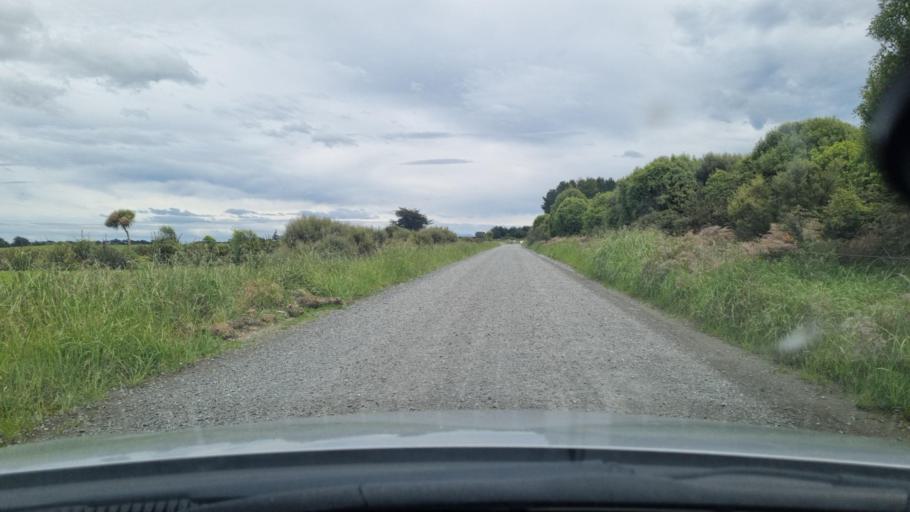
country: NZ
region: Southland
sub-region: Invercargill City
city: Invercargill
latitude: -46.4061
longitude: 168.2765
